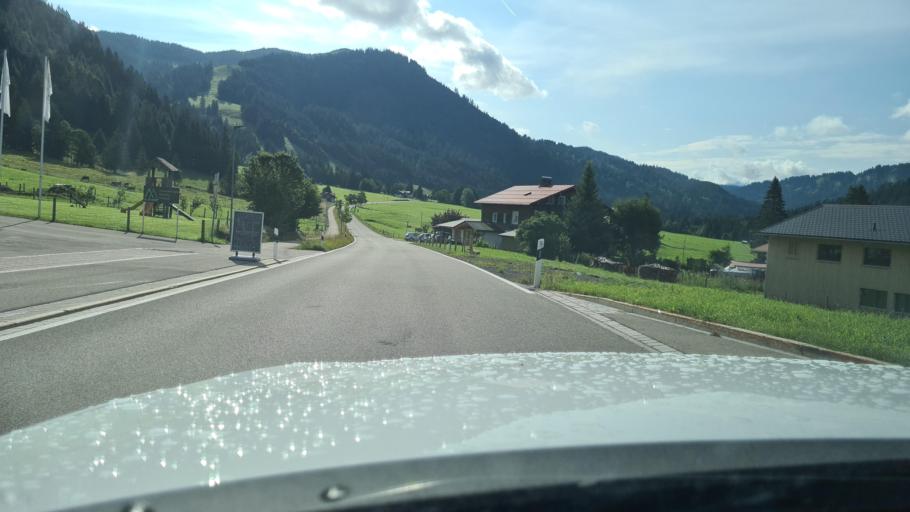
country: DE
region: Bavaria
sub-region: Swabia
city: Balderschwang
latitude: 47.4625
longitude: 10.1192
